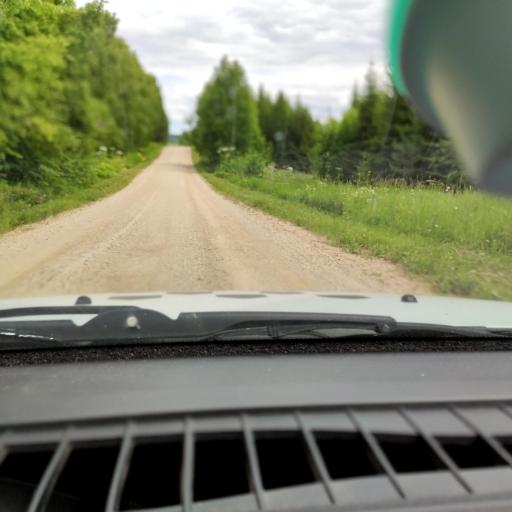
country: RU
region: Perm
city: Suksun
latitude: 57.2126
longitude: 57.6762
